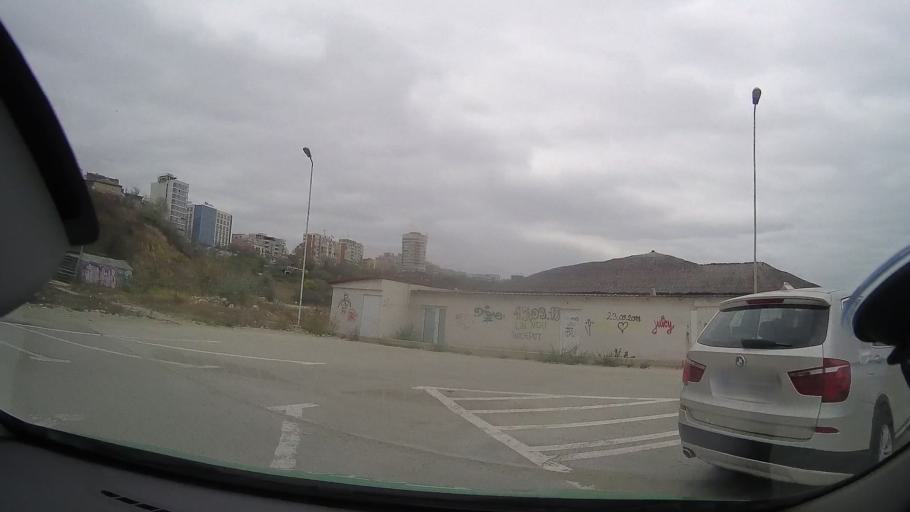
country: RO
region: Constanta
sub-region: Municipiul Constanta
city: Constanta
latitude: 44.1776
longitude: 28.6588
